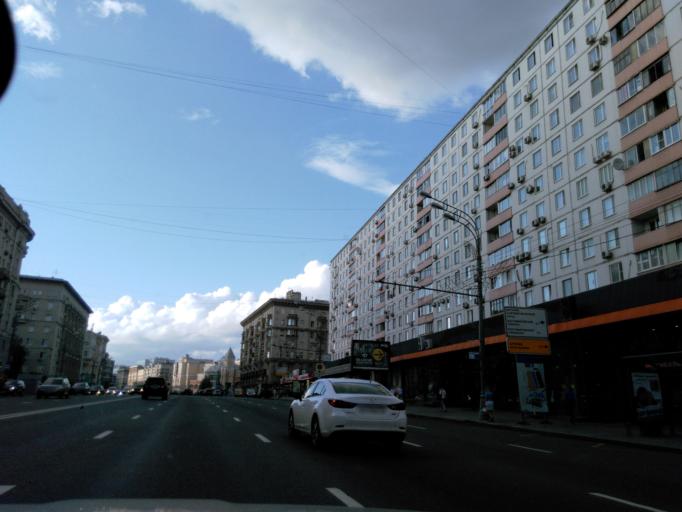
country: RU
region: Moscow
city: Taganskiy
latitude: 55.7534
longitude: 37.6566
